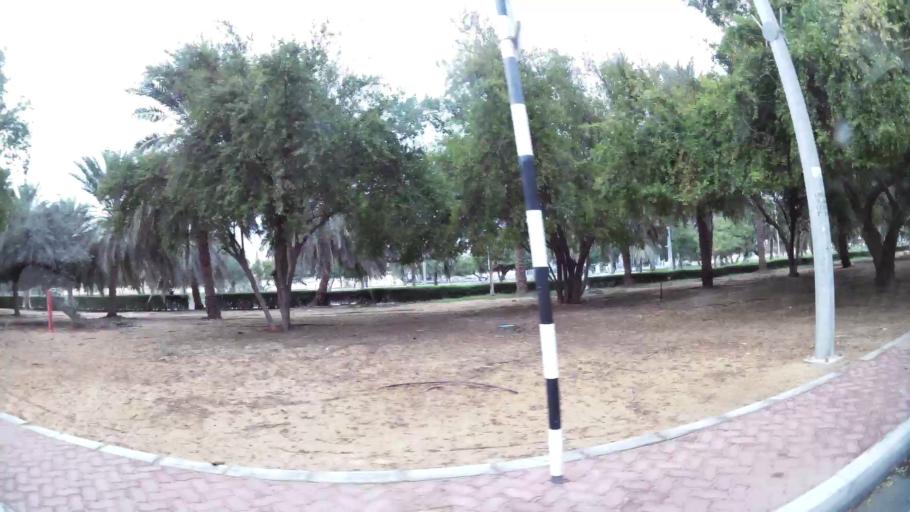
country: AE
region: Abu Dhabi
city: Abu Dhabi
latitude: 24.4445
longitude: 54.3902
